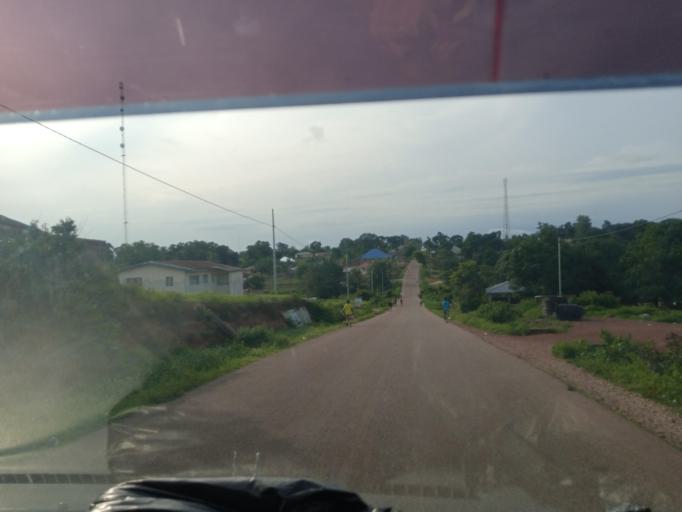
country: SL
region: Southern Province
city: Largo
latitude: 8.1967
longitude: -12.0583
